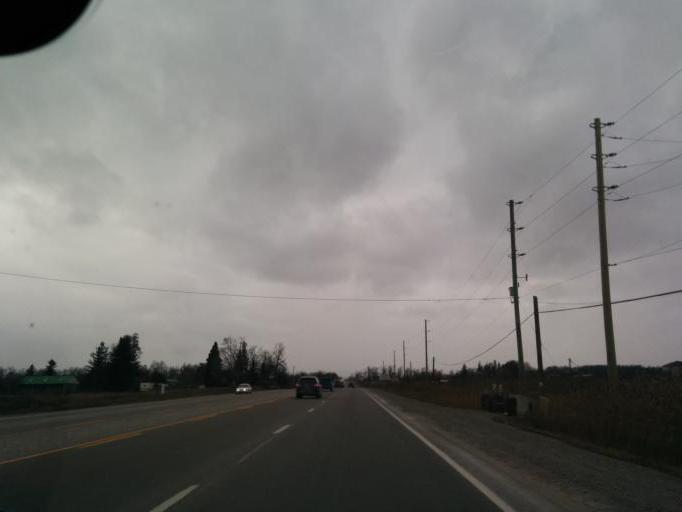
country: CA
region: Ontario
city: Brampton
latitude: 43.7473
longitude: -79.8432
